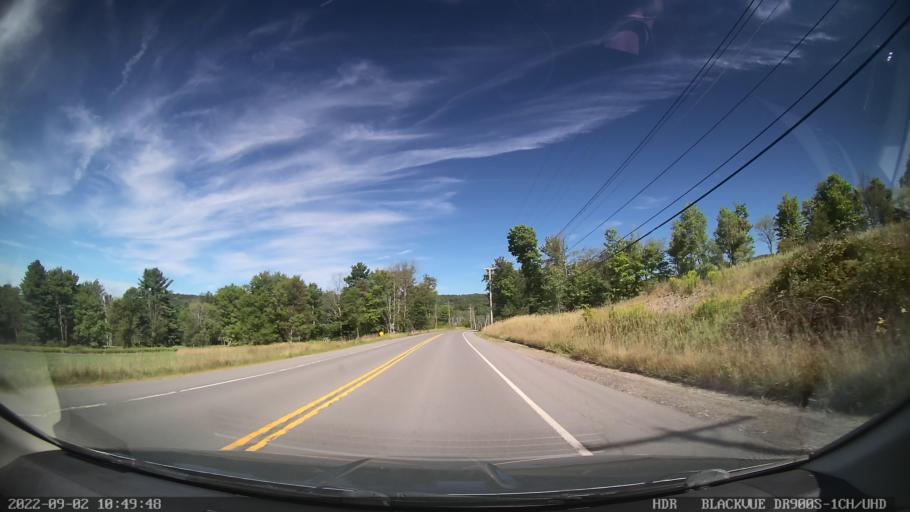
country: US
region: Pennsylvania
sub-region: Tioga County
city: Blossburg
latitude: 41.6049
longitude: -77.1143
